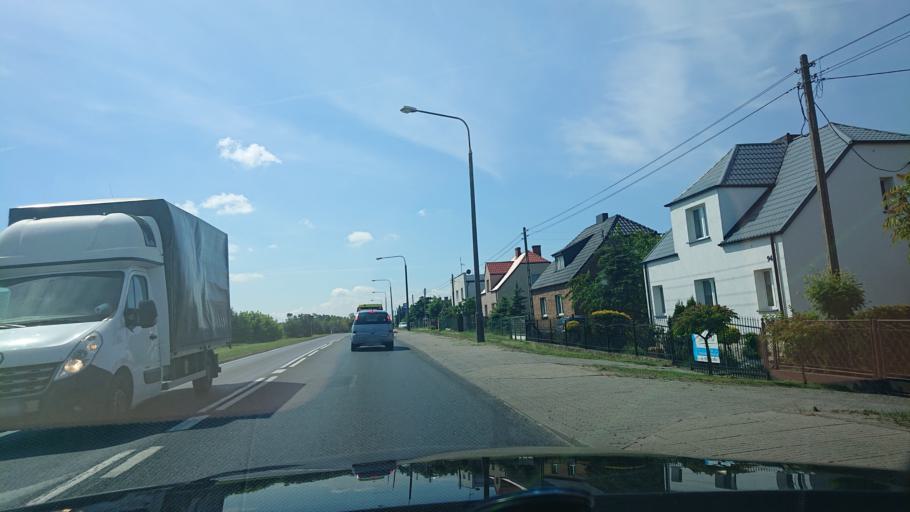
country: PL
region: Greater Poland Voivodeship
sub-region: Powiat gnieznienski
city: Gniezno
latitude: 52.5110
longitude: 17.5950
